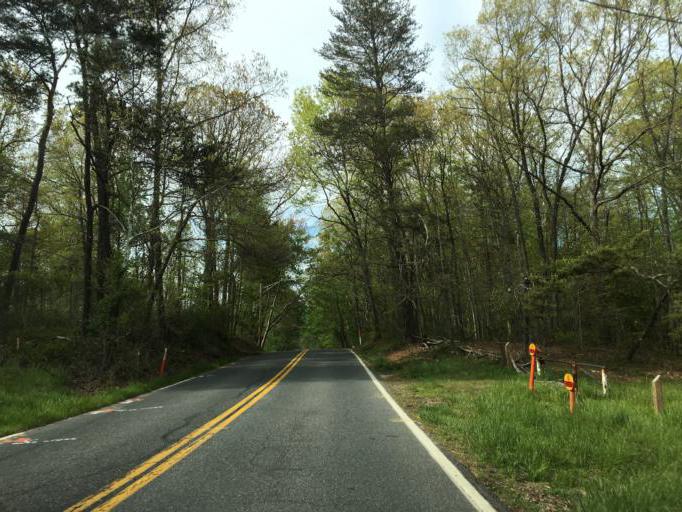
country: US
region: Maryland
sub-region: Howard County
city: Elkridge
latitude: 39.1949
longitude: -76.7024
